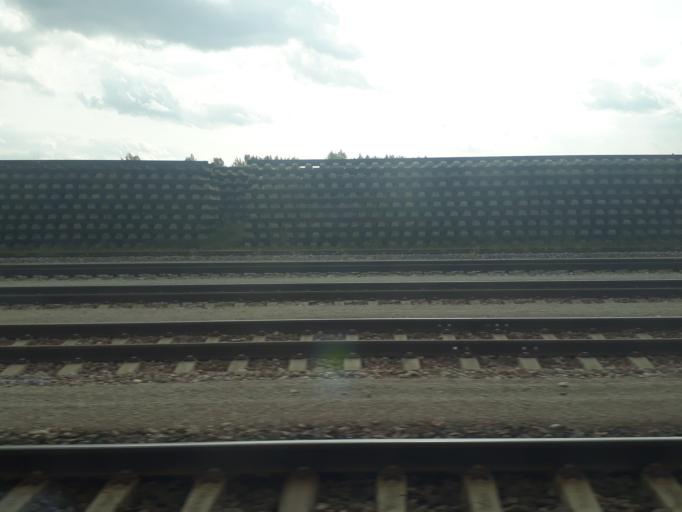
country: EE
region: Laeaene-Virumaa
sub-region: Tapa vald
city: Tapa
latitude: 59.2638
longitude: 25.9370
